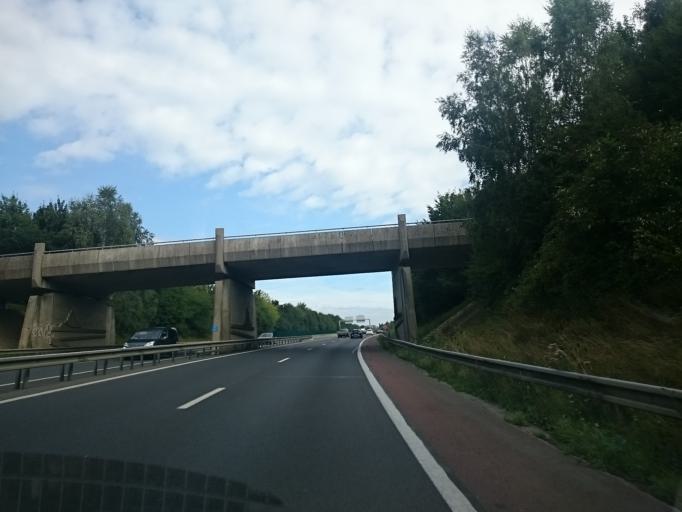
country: FR
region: Lower Normandy
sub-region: Departement de la Manche
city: Le Val-Saint-Pere
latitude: 48.6714
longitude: -1.3727
